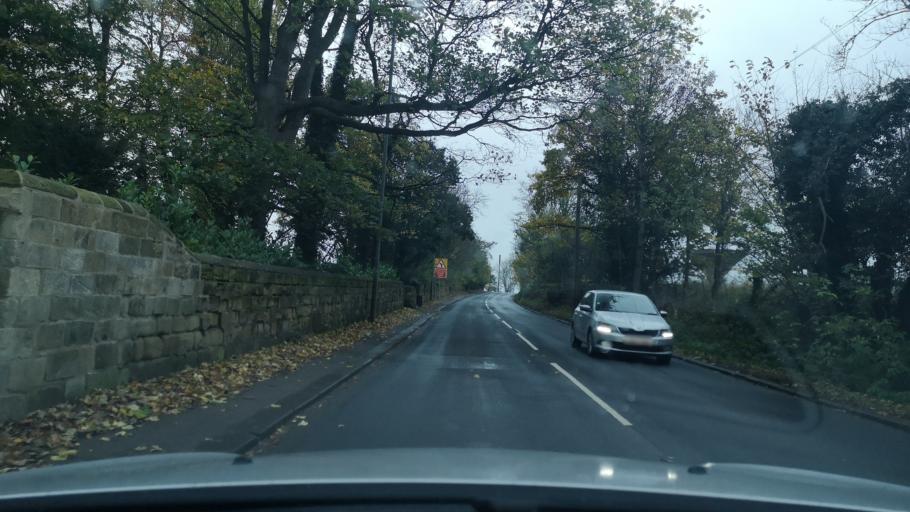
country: GB
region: England
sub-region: City and Borough of Wakefield
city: Low Ackworth
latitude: 53.6639
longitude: -1.3264
